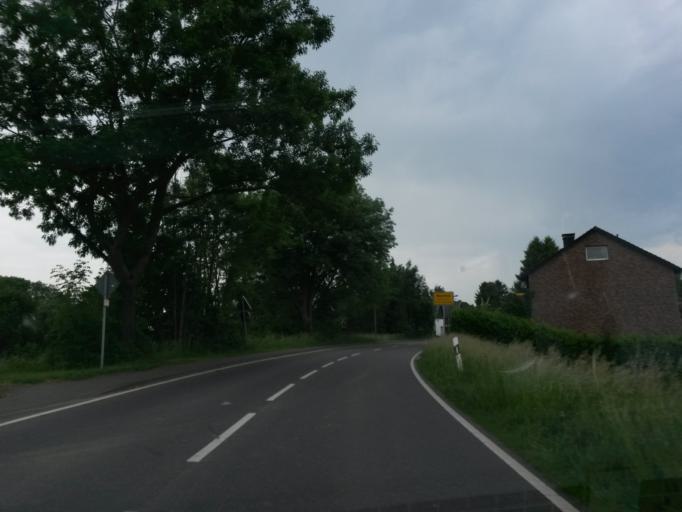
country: DE
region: North Rhine-Westphalia
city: Lohmar
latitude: 50.8871
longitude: 7.2355
